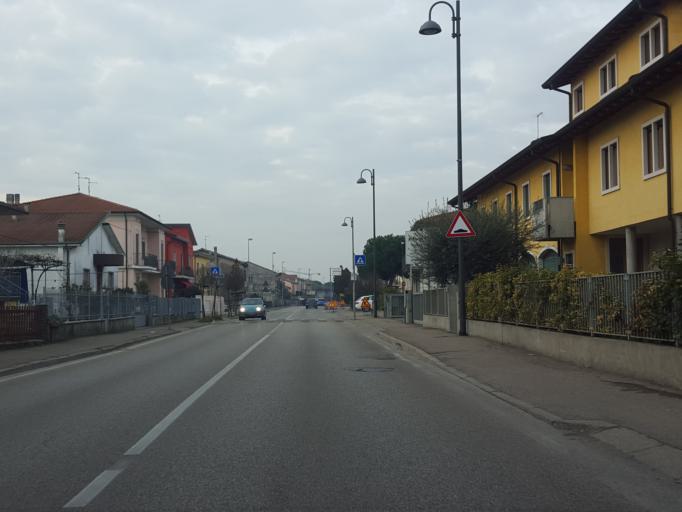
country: IT
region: Veneto
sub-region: Provincia di Verona
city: San Bonifacio
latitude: 45.3985
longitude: 11.2984
